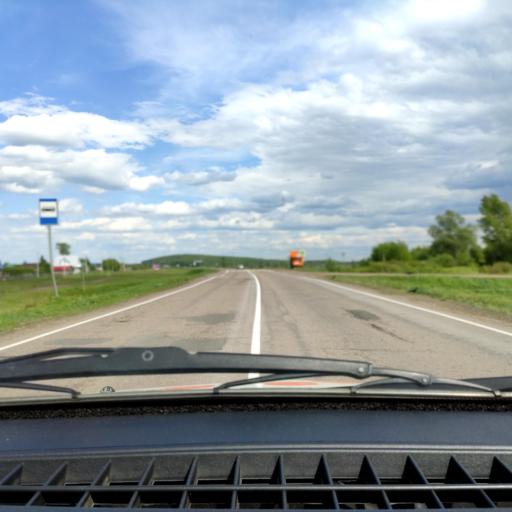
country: RU
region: Bashkortostan
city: Krasnaya Gorka
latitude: 55.0583
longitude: 56.5628
